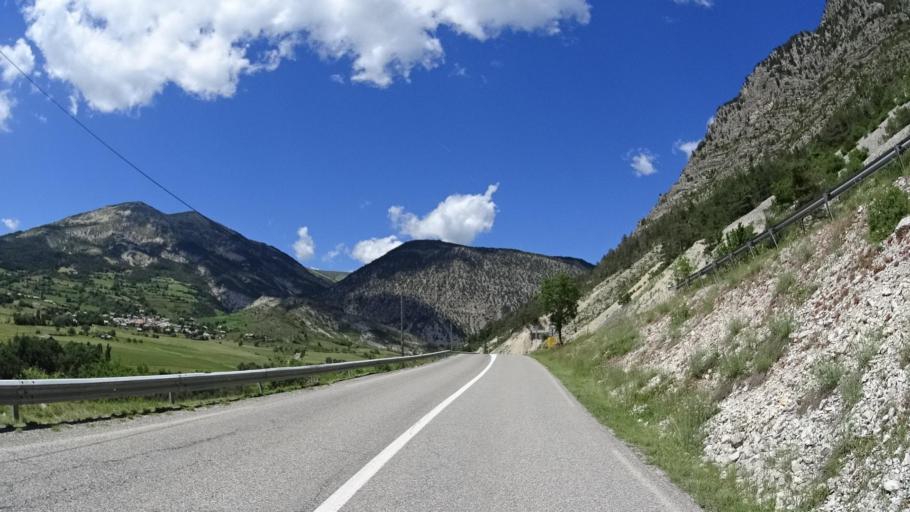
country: FR
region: Provence-Alpes-Cote d'Azur
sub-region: Departement des Alpes-de-Haute-Provence
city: Annot
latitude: 44.0882
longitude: 6.5666
